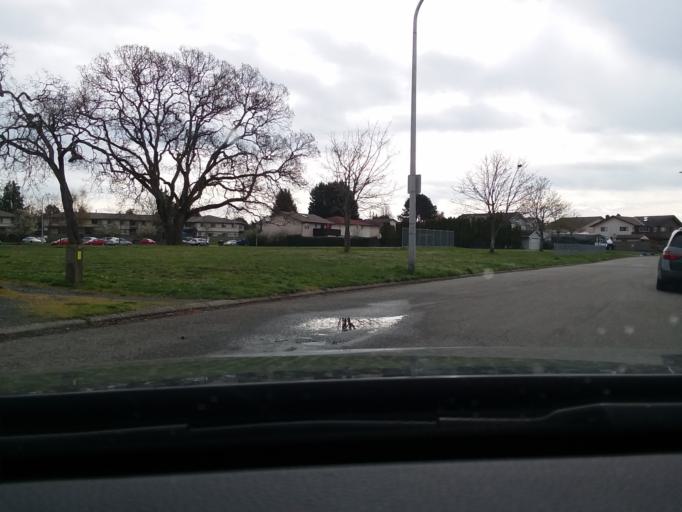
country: CA
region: British Columbia
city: Oak Bay
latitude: 48.4742
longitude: -123.3273
